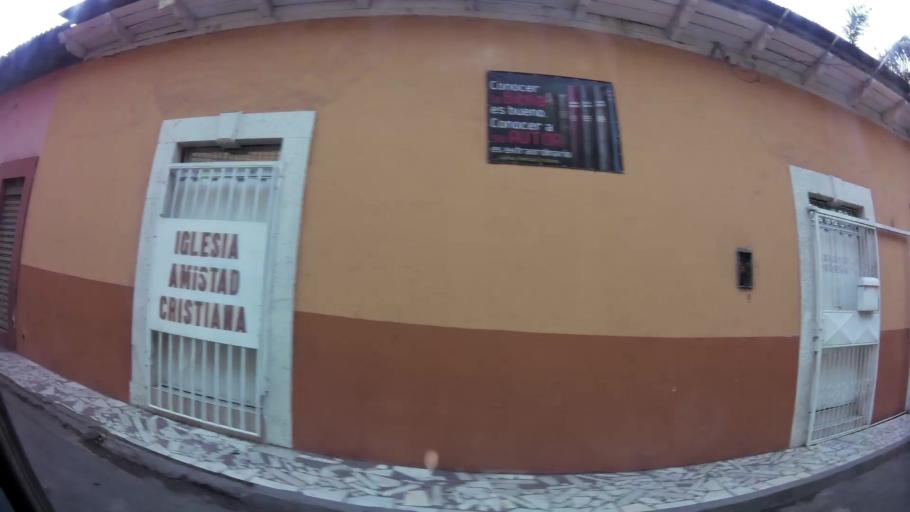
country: HN
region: Francisco Morazan
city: Tegucigalpa
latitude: 14.0988
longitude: -87.2074
